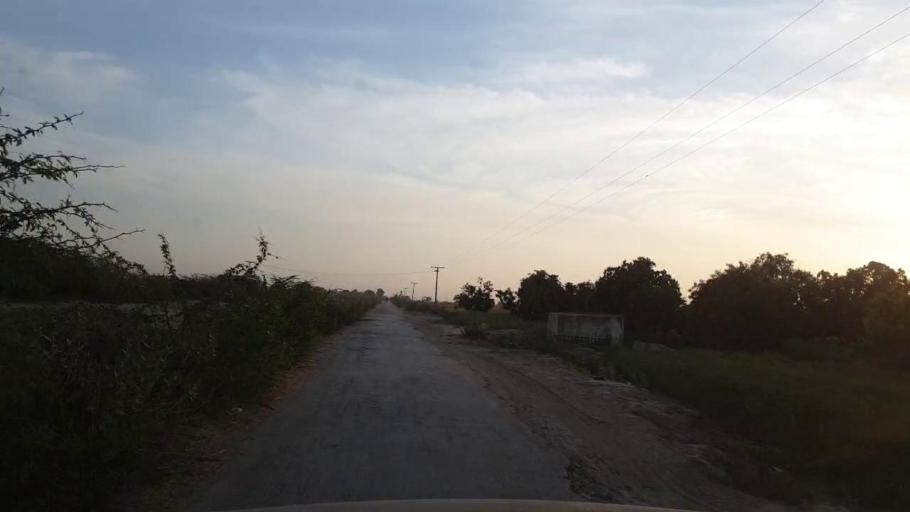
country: PK
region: Sindh
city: Kunri
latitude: 25.1469
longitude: 69.5818
